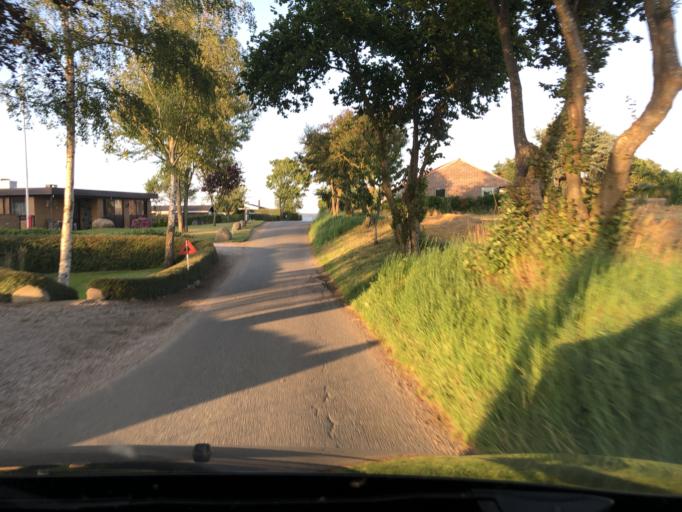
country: DK
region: South Denmark
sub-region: Vejle Kommune
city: Brejning
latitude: 55.6567
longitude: 9.7336
